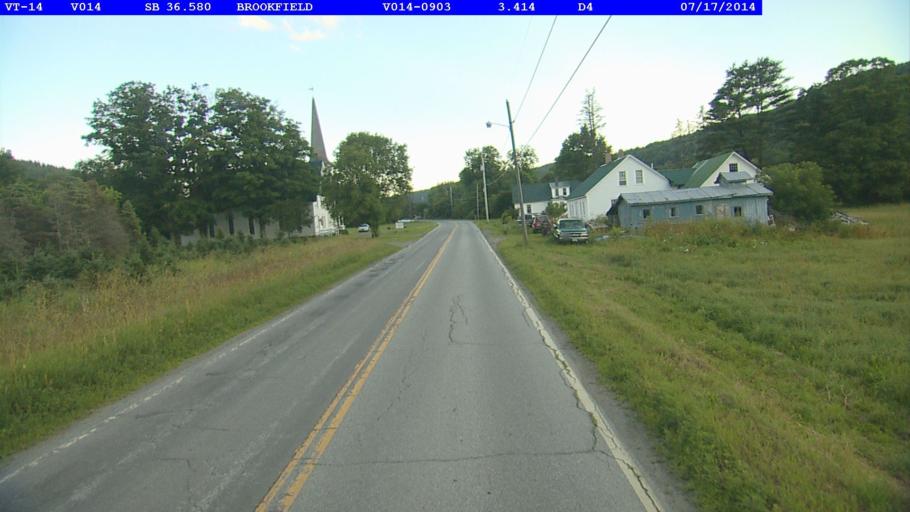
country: US
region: Vermont
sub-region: Orange County
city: Williamstown
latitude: 44.0262
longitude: -72.5712
